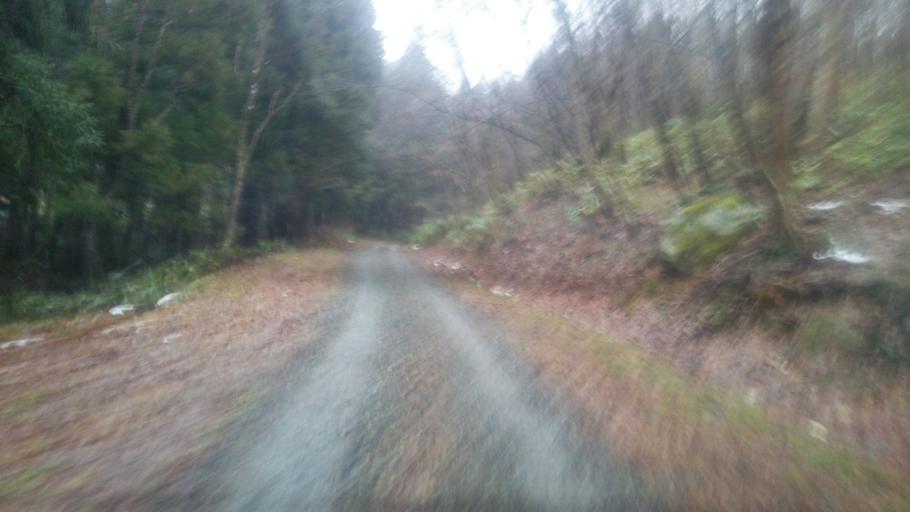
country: JP
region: Fukushima
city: Kitakata
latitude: 37.5764
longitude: 139.9790
